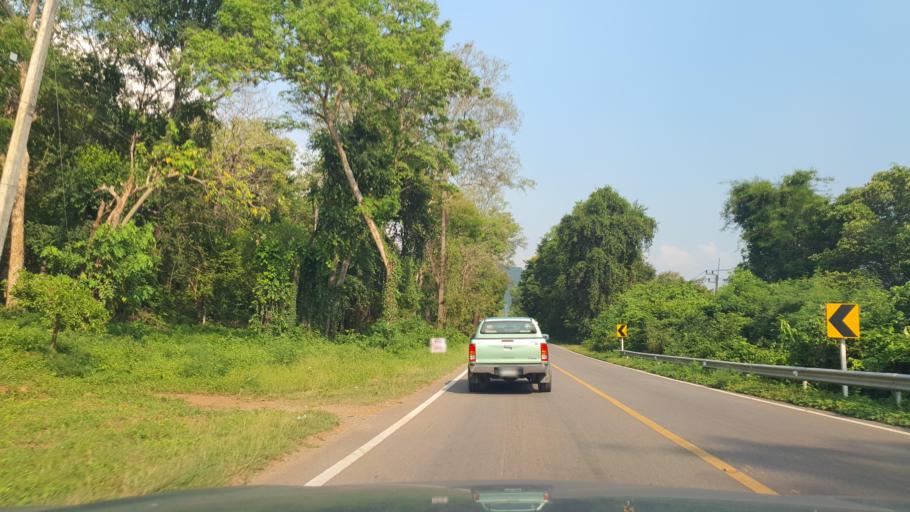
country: TH
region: Kanchanaburi
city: Sai Yok
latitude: 14.2777
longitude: 99.2253
